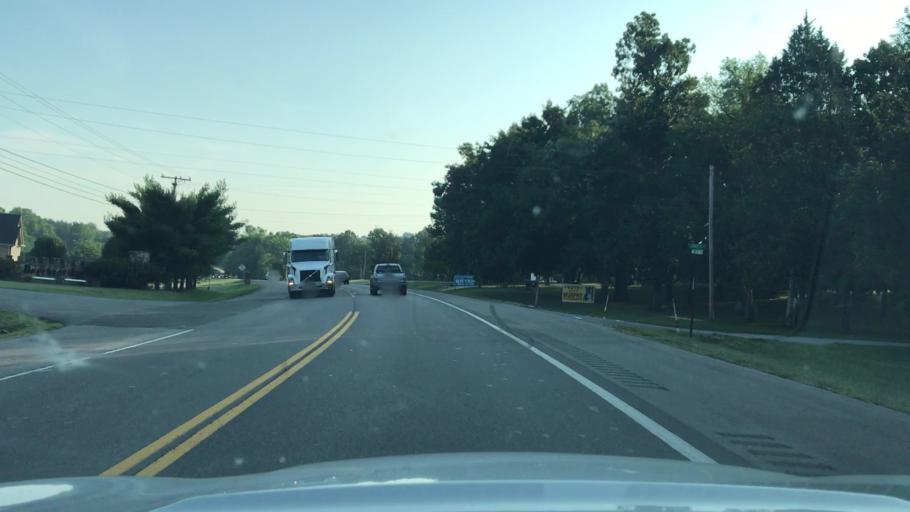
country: US
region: Tennessee
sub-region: Wilson County
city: Rural Hill
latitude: 36.1413
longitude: -86.5171
